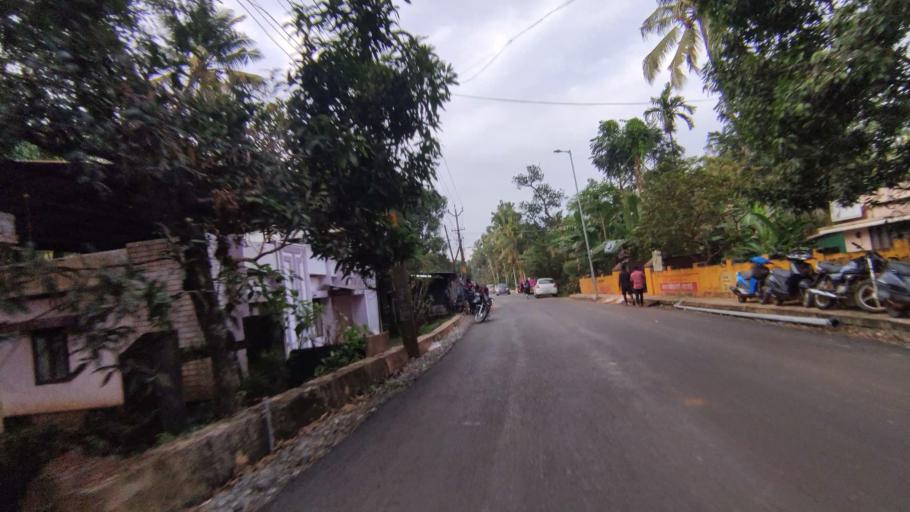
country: IN
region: Kerala
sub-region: Kottayam
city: Kottayam
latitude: 9.6353
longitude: 76.4961
